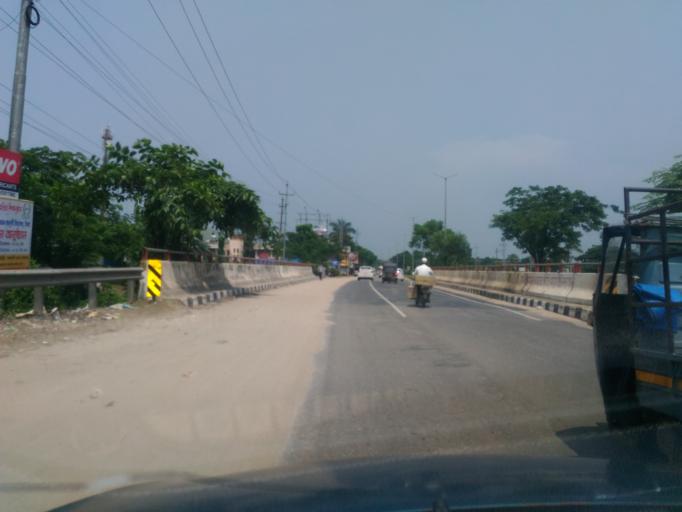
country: IN
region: Assam
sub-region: Kamrup
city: Soalkuchi
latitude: 26.1374
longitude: 91.6292
